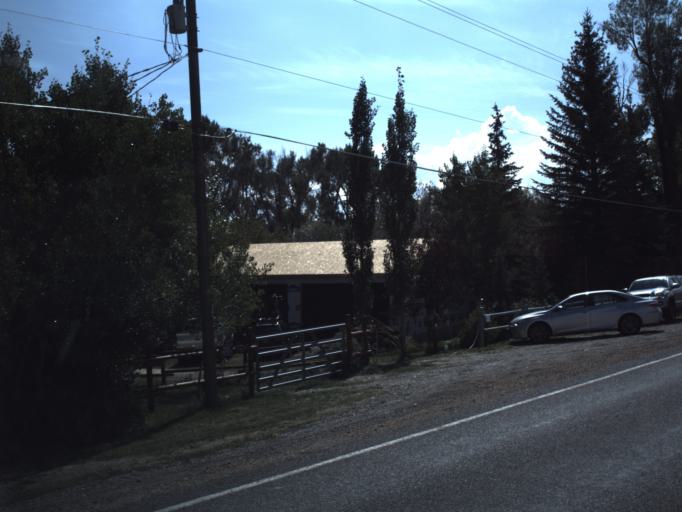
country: US
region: Idaho
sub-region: Bear Lake County
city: Paris
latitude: 41.9323
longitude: -111.3952
